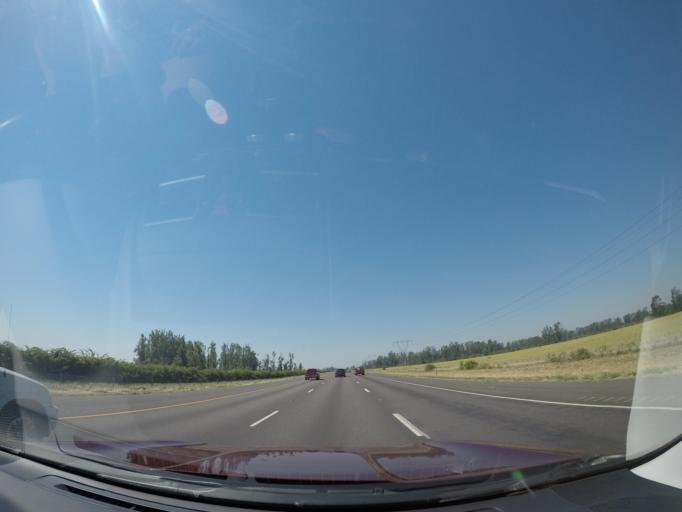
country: US
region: Oregon
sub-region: Marion County
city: Gervais
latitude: 45.1117
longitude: -122.9210
